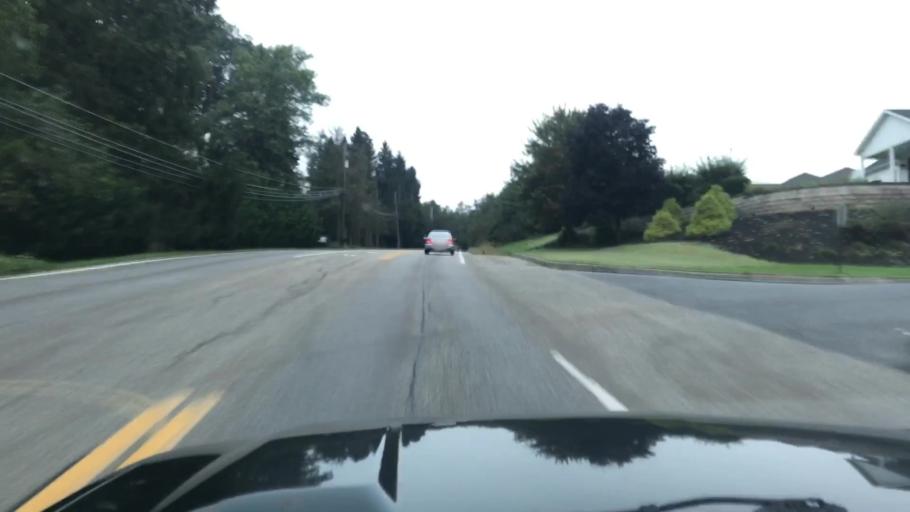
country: US
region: Pennsylvania
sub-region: Cumberland County
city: Shiremanstown
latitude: 40.1845
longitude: -76.9312
